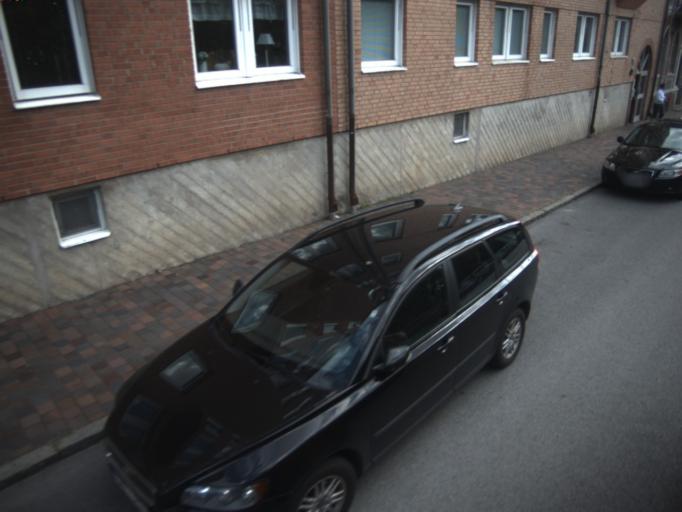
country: SE
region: Skane
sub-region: Helsingborg
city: Helsingborg
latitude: 56.0430
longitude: 12.7074
